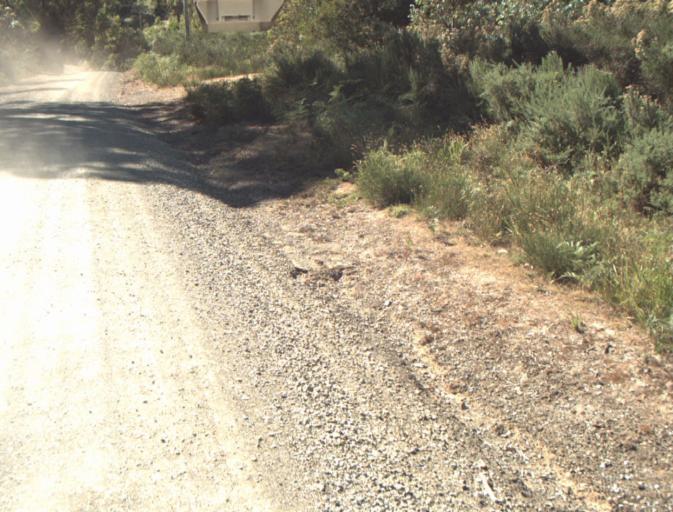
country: AU
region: Tasmania
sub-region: Launceston
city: Newstead
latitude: -41.3228
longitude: 147.3299
